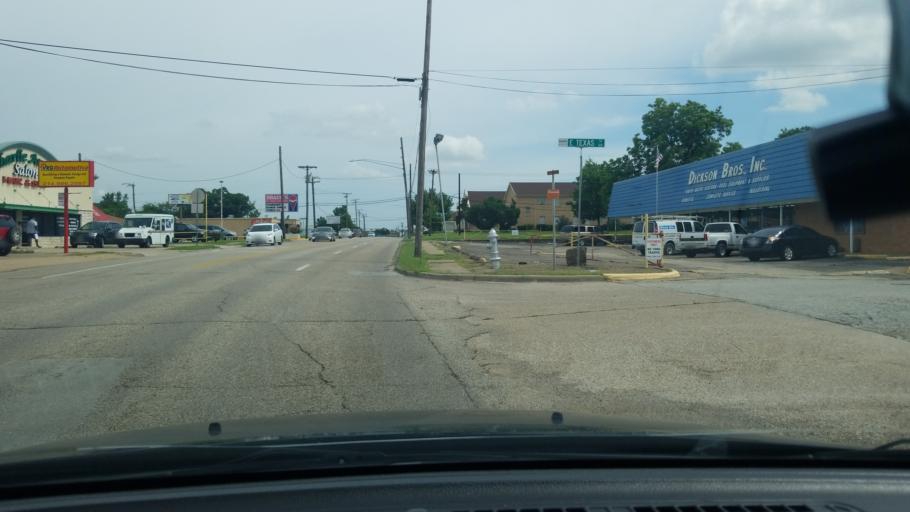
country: US
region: Texas
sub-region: Dallas County
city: Mesquite
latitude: 32.7676
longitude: -96.5991
